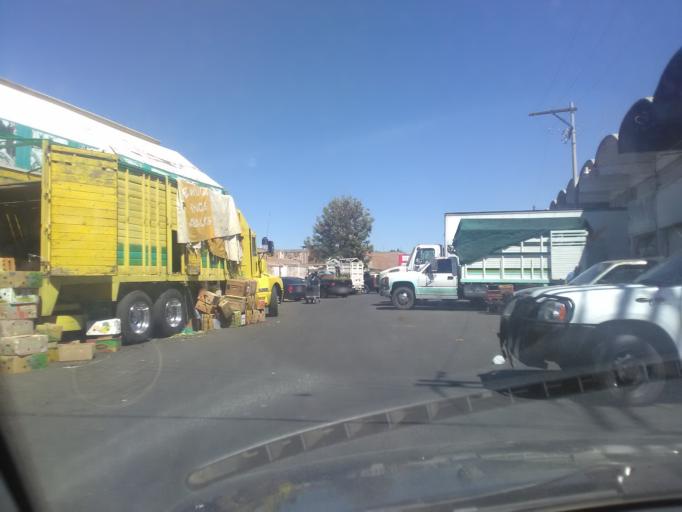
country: MX
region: Durango
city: Victoria de Durango
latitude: 24.0158
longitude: -104.6621
